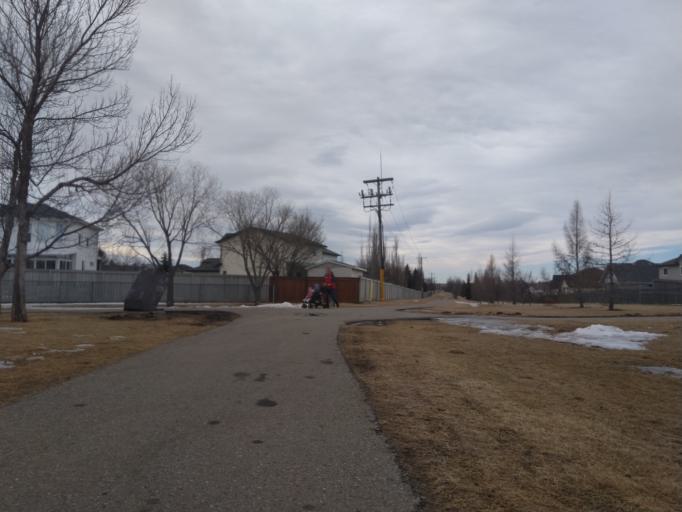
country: CA
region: Alberta
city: Calgary
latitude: 51.1631
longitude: -114.0480
